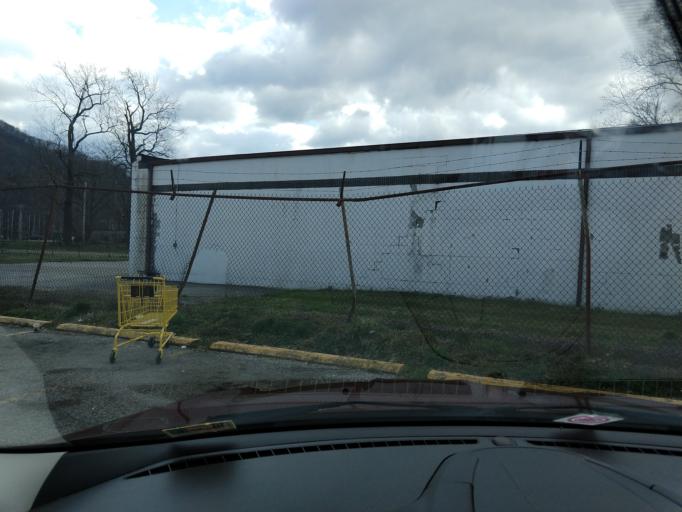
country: US
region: West Virginia
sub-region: Kanawha County
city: Marmet
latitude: 38.2469
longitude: -81.5680
